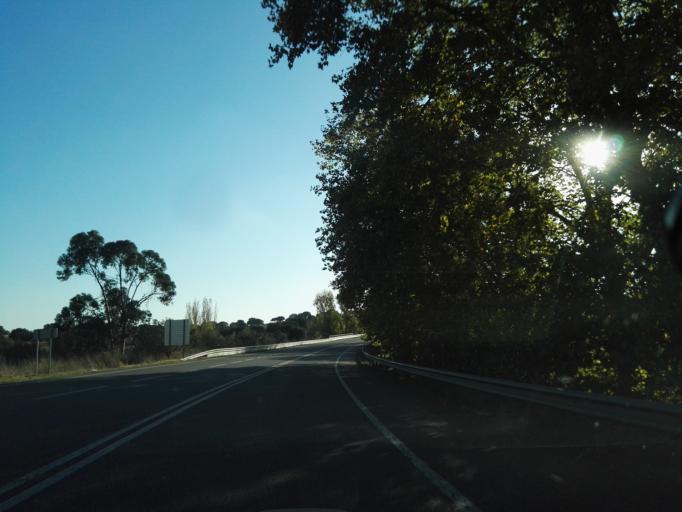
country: PT
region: Evora
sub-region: Vila Vicosa
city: Vila Vicosa
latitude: 38.8324
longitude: -7.4042
